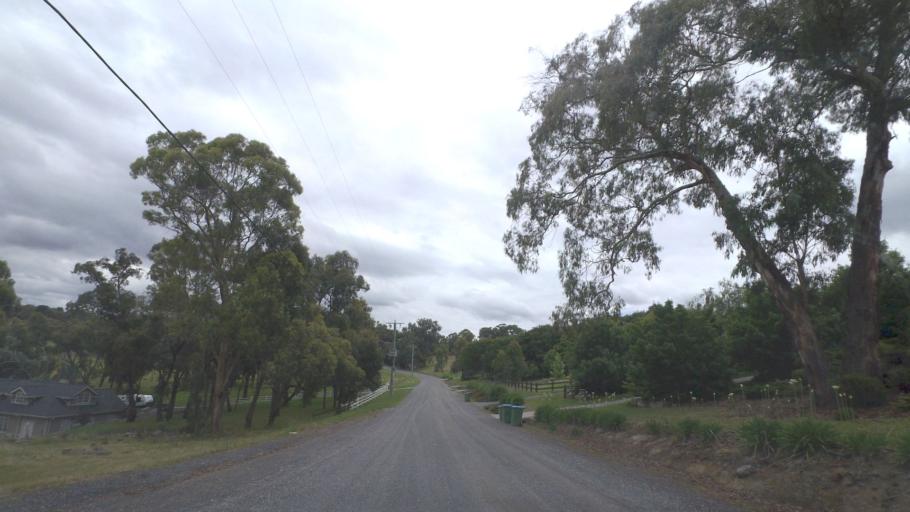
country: AU
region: Victoria
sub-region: Maroondah
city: Warranwood
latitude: -37.7660
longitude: 145.2443
